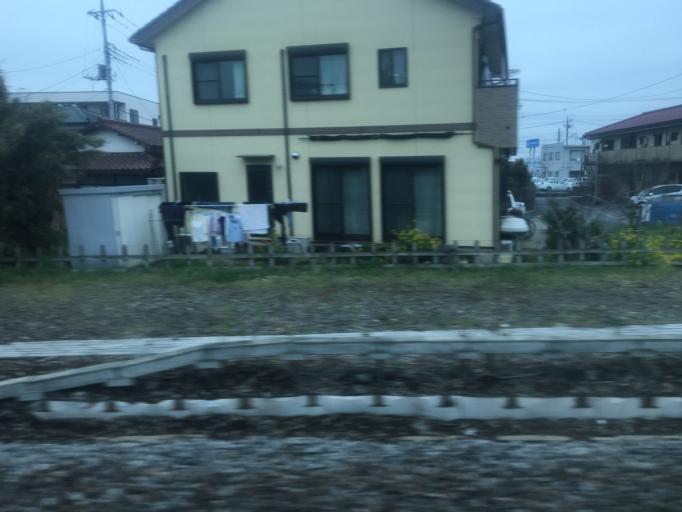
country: JP
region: Saitama
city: Okegawa
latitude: 36.0231
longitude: 139.5405
